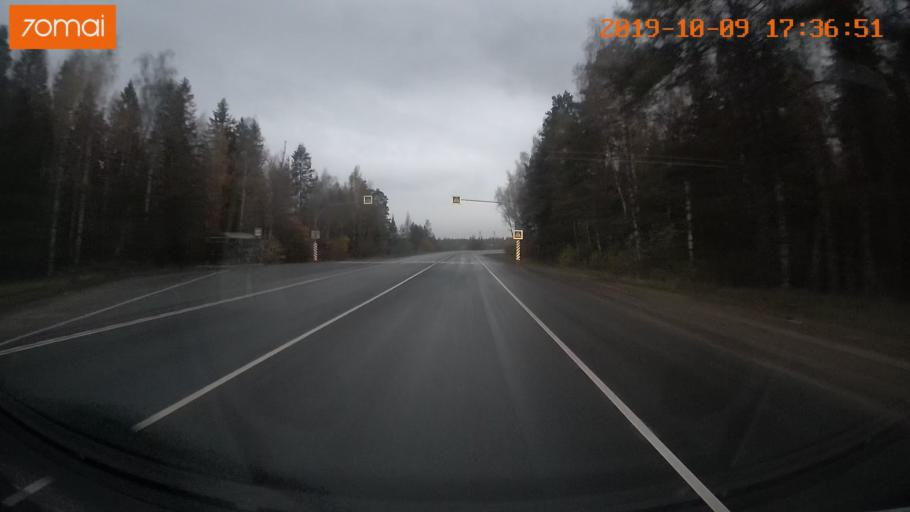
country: RU
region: Ivanovo
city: Bogorodskoye
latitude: 57.0728
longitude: 40.9917
